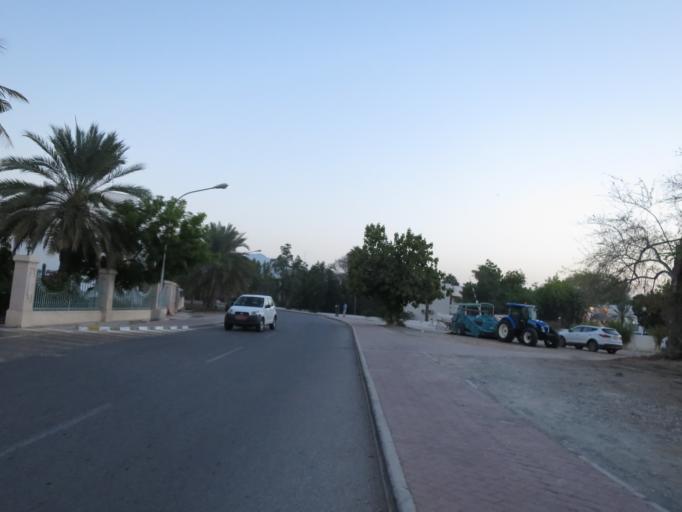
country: OM
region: Muhafazat Masqat
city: Bawshar
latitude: 23.6078
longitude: 58.4433
